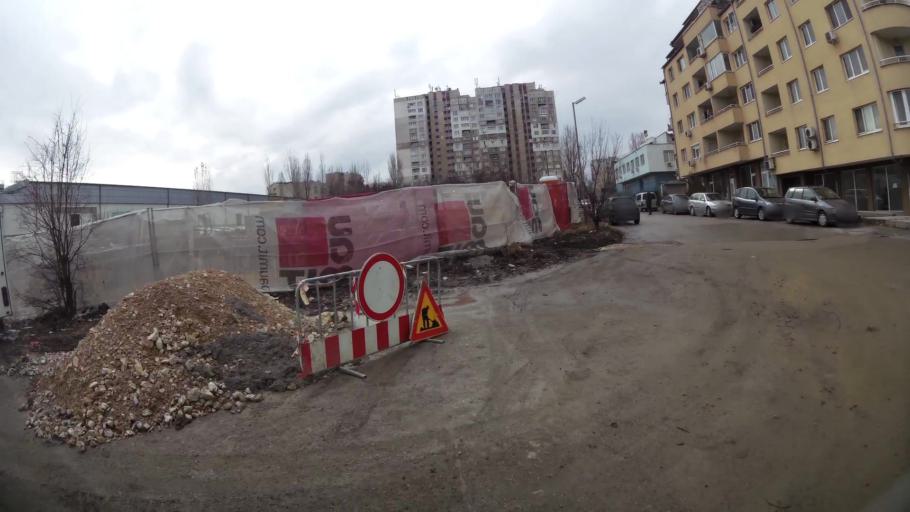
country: BG
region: Sofiya
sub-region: Obshtina Bozhurishte
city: Bozhurishte
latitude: 42.7223
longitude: 23.2527
